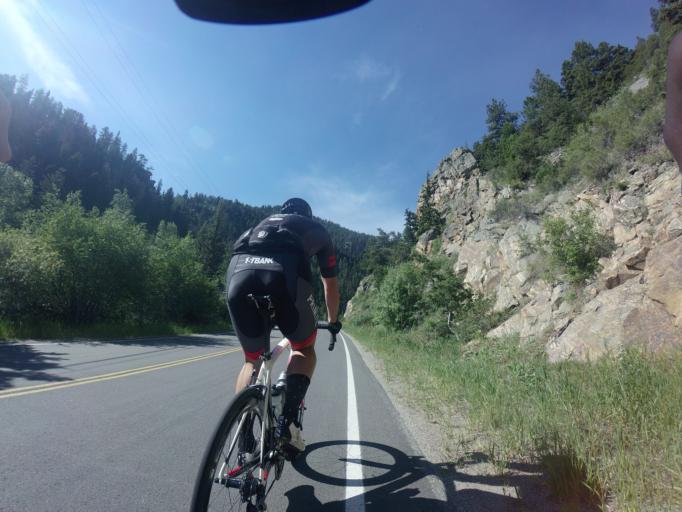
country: US
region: Colorado
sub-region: Clear Creek County
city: Idaho Springs
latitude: 39.7189
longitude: -105.5703
